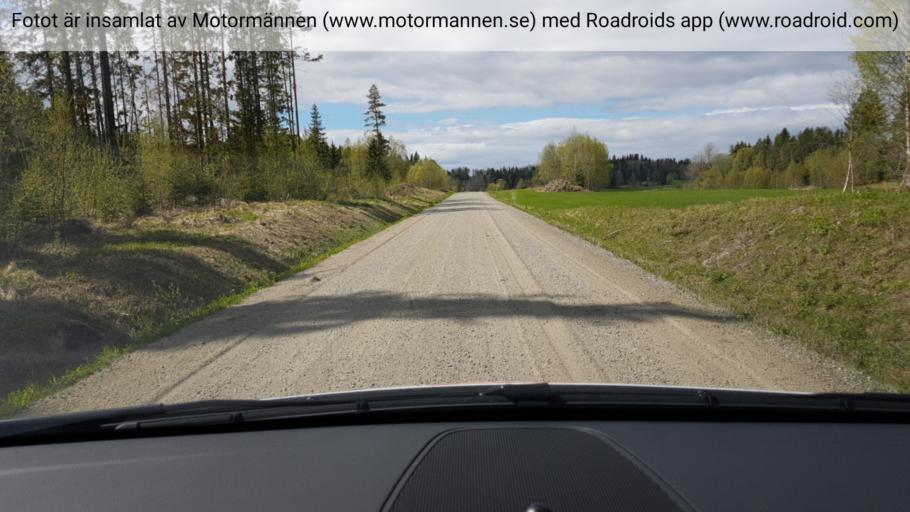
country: SE
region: Jaemtland
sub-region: OEstersunds Kommun
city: Brunflo
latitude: 62.9517
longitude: 14.9349
